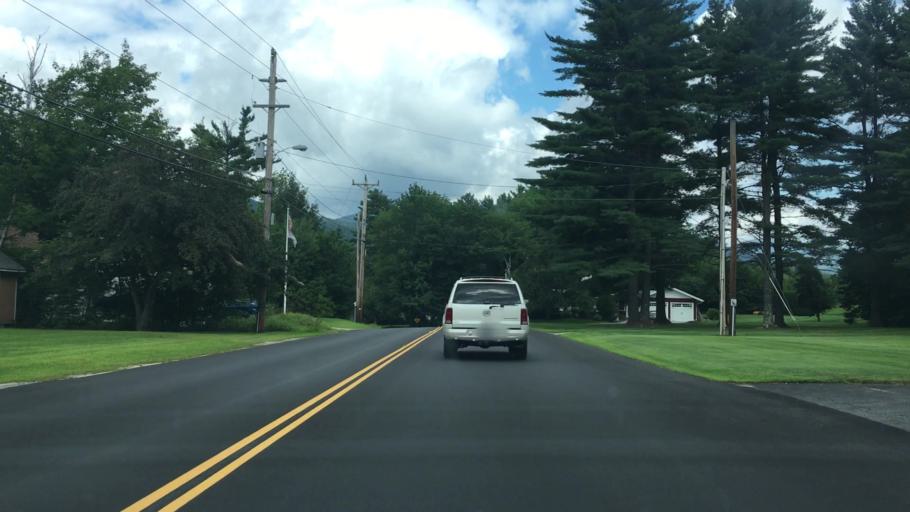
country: US
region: New Hampshire
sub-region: Grafton County
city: Woodstock
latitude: 44.0445
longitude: -71.6832
